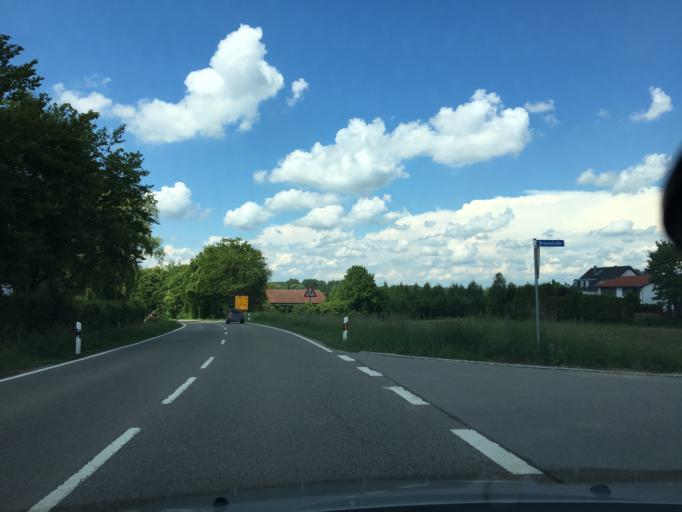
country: DE
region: Bavaria
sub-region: Upper Bavaria
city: Fahrenzhausen
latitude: 48.3409
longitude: 11.5723
